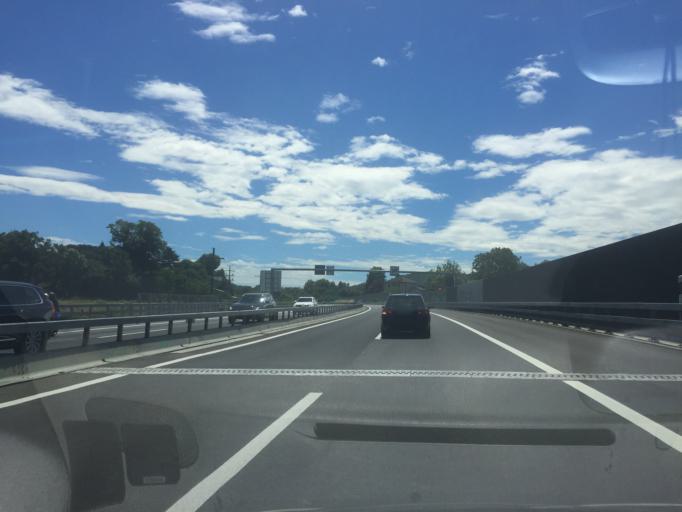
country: CH
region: Ticino
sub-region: Mendrisio District
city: Mendrisio
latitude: 45.8636
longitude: 8.9704
